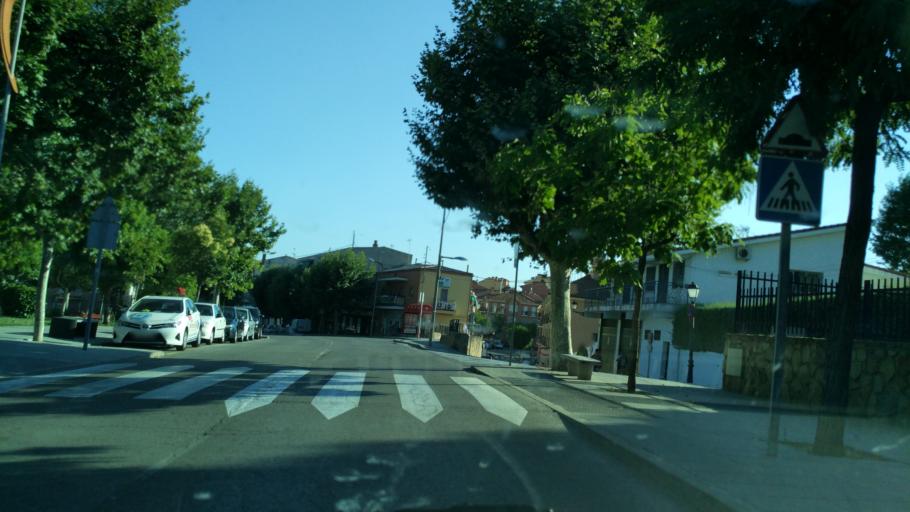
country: ES
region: Madrid
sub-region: Provincia de Madrid
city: San Agustin de Guadalix
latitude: 40.6810
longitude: -3.6138
